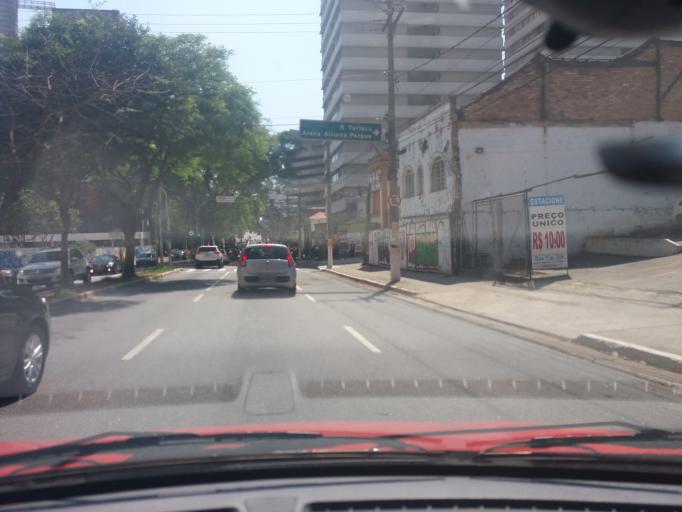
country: BR
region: Sao Paulo
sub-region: Sao Paulo
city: Sao Paulo
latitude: -23.5279
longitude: -46.6834
